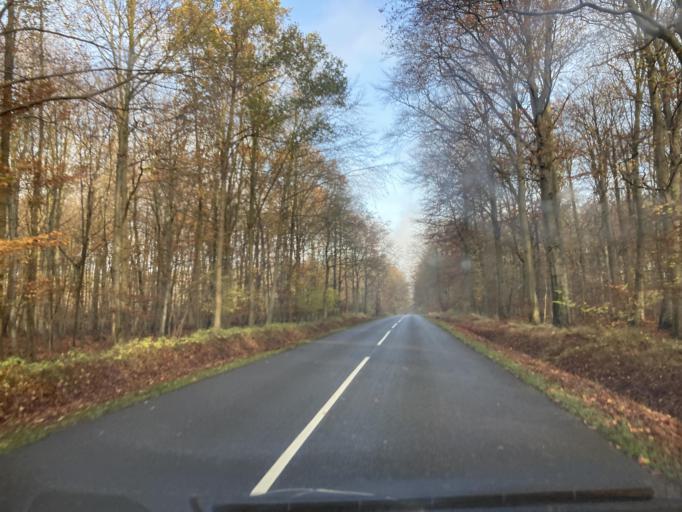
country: DK
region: Zealand
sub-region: Lolland Kommune
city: Rodby
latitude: 54.7643
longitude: 11.3587
